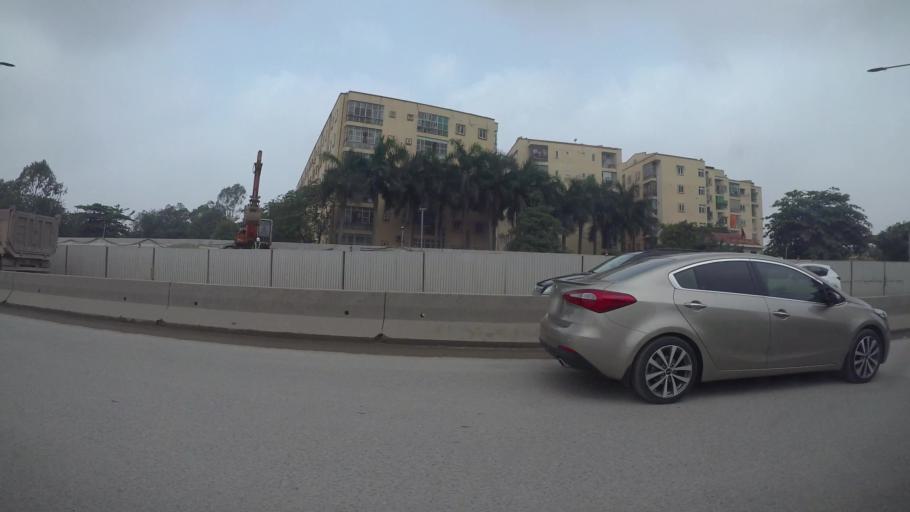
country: VN
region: Ha Noi
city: Tay Ho
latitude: 21.0829
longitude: 105.7882
